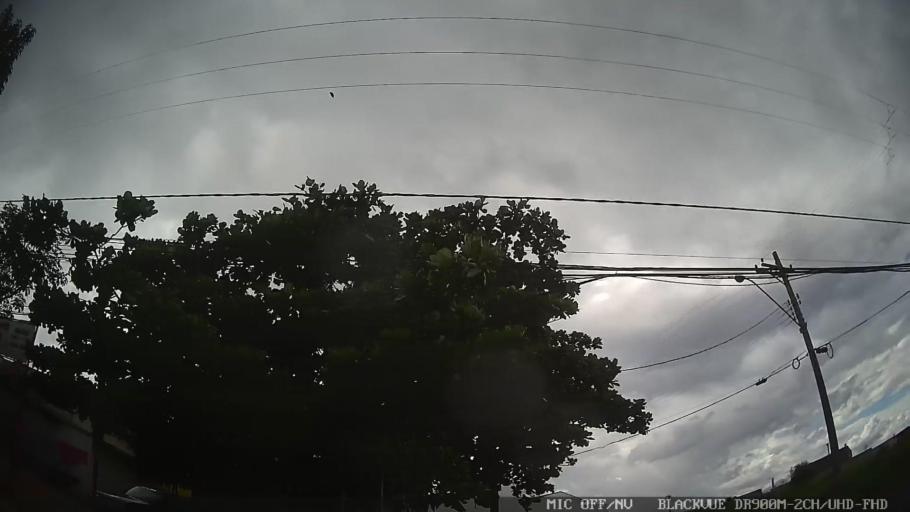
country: BR
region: Sao Paulo
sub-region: Jaguariuna
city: Jaguariuna
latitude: -22.6803
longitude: -46.9914
